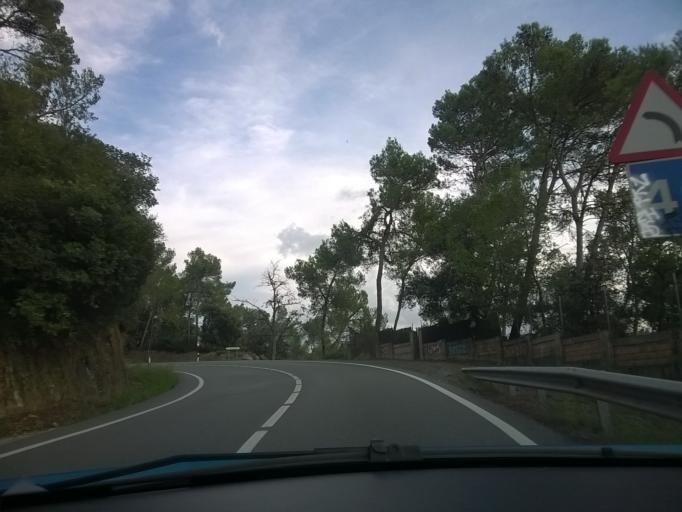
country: ES
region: Catalonia
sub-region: Provincia de Barcelona
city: Sant Cugat del Valles
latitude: 41.4462
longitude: 2.0959
